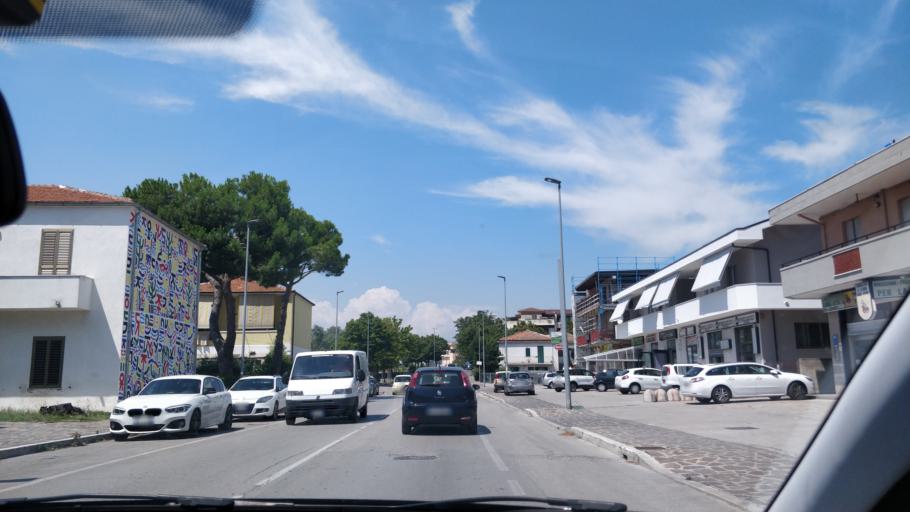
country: IT
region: Abruzzo
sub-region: Provincia di Chieti
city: Francavilla al Mare
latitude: 42.4231
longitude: 14.2815
